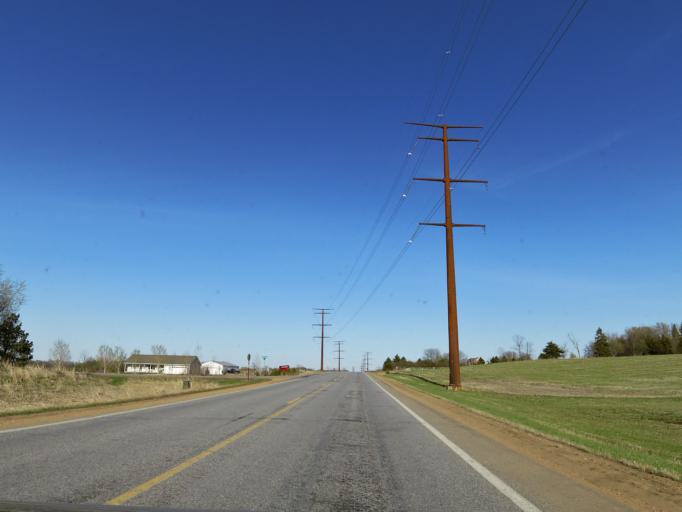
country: US
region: Minnesota
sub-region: Le Sueur County
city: New Prague
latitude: 44.5726
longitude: -93.4935
